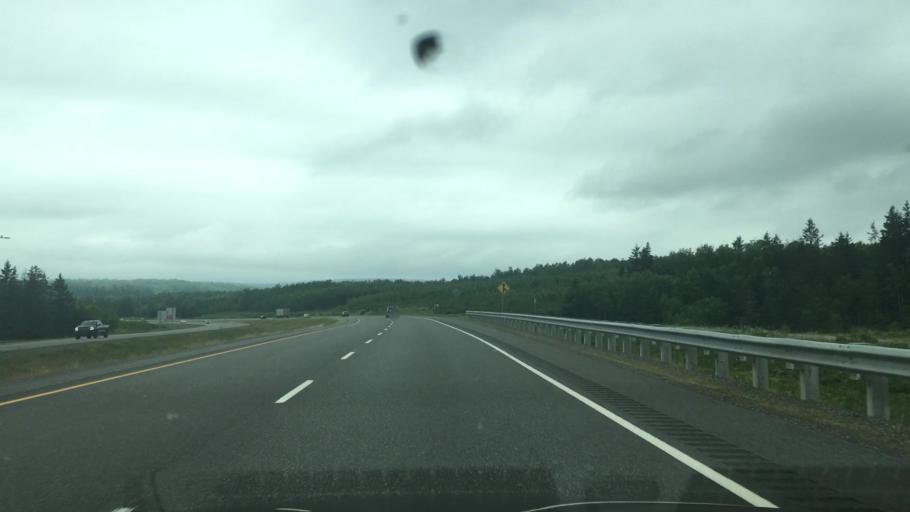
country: CA
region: Nova Scotia
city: Truro
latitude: 45.4402
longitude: -63.5855
